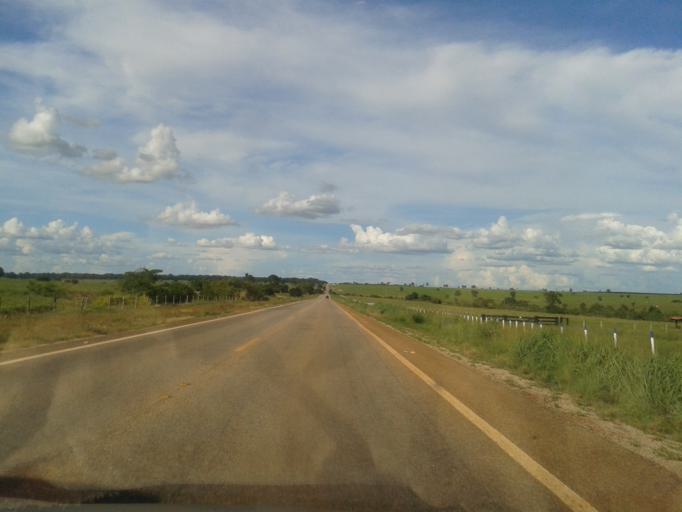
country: BR
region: Goias
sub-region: Mozarlandia
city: Mozarlandia
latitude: -14.3560
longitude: -50.4245
